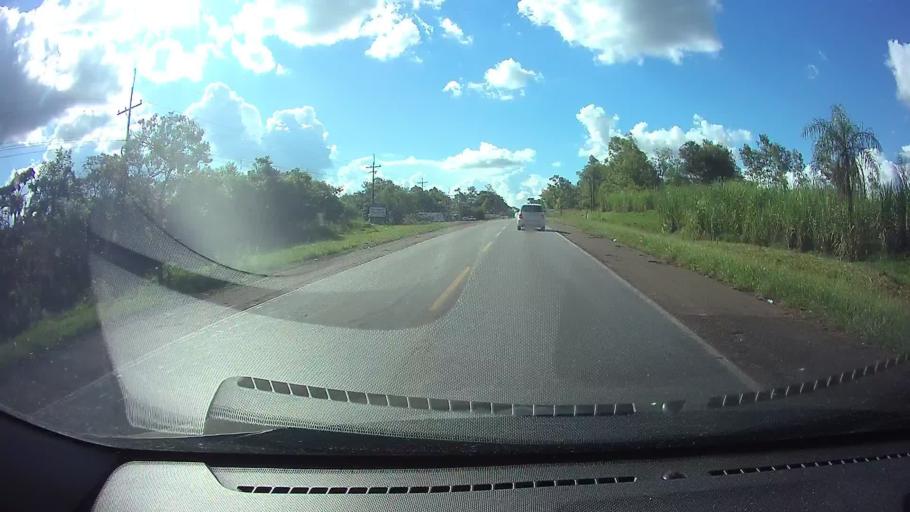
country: PY
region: Cordillera
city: Eusebio Ayala
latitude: -25.4215
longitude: -56.9243
